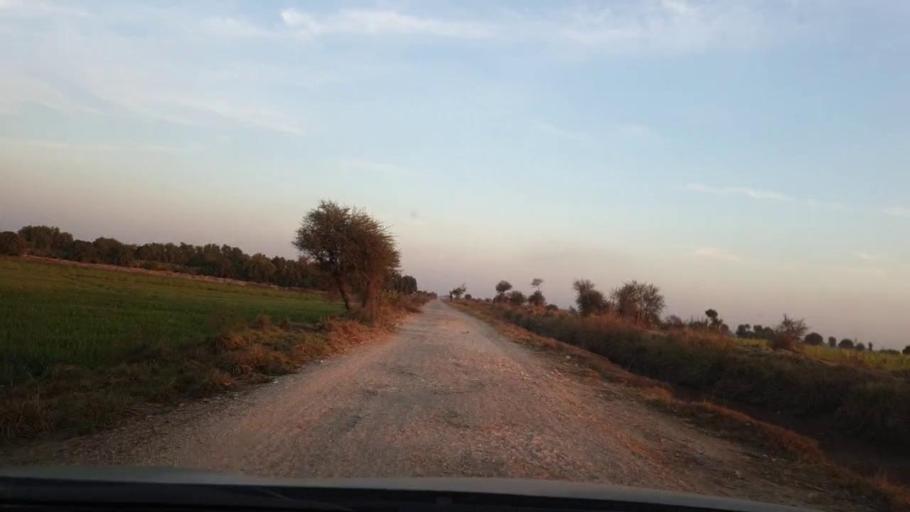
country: PK
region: Sindh
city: Tando Allahyar
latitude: 25.5853
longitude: 68.7202
